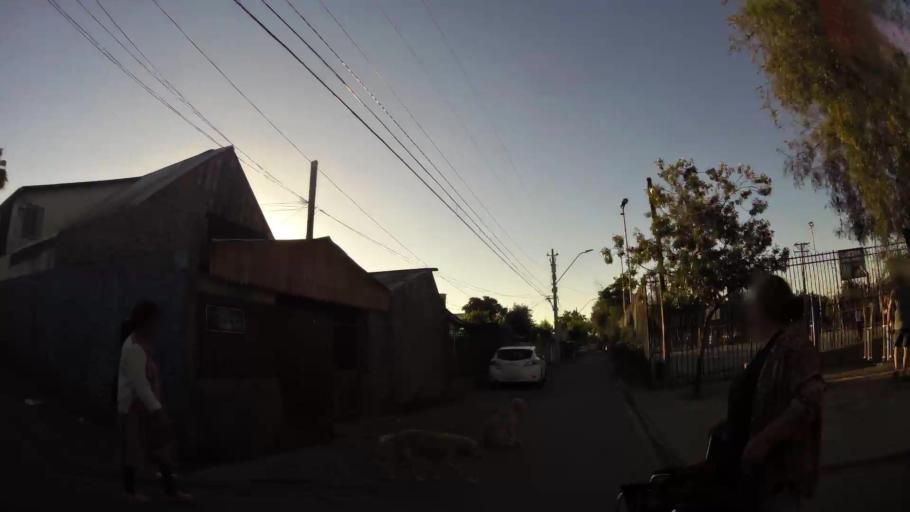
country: CL
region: Santiago Metropolitan
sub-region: Provincia de Maipo
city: San Bernardo
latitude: -33.5850
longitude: -70.6928
